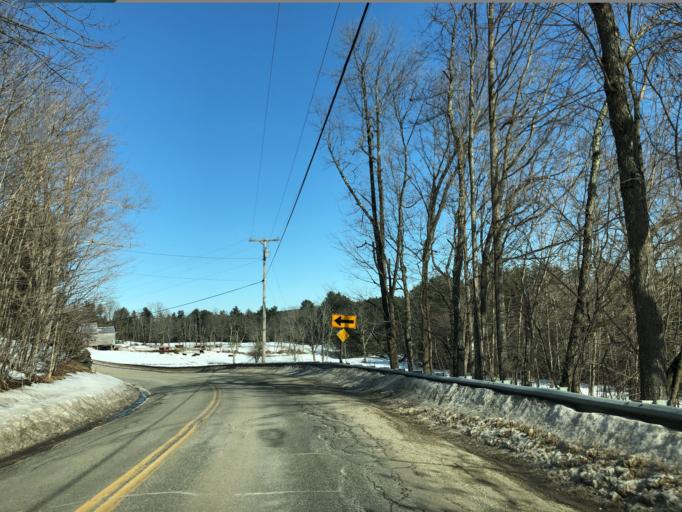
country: US
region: Maine
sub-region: Oxford County
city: Hebron
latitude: 44.1894
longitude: -70.3618
